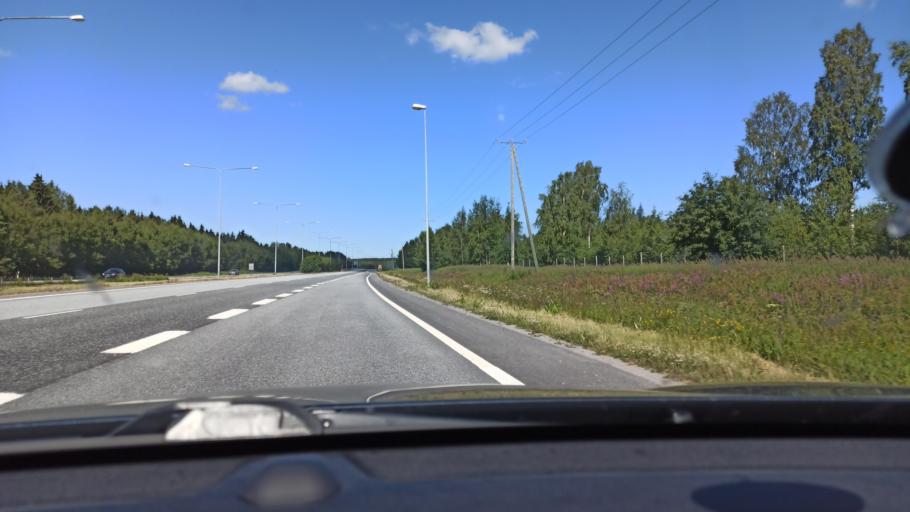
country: FI
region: Ostrobothnia
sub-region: Vaasa
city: Ristinummi
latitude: 63.0372
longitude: 21.7372
